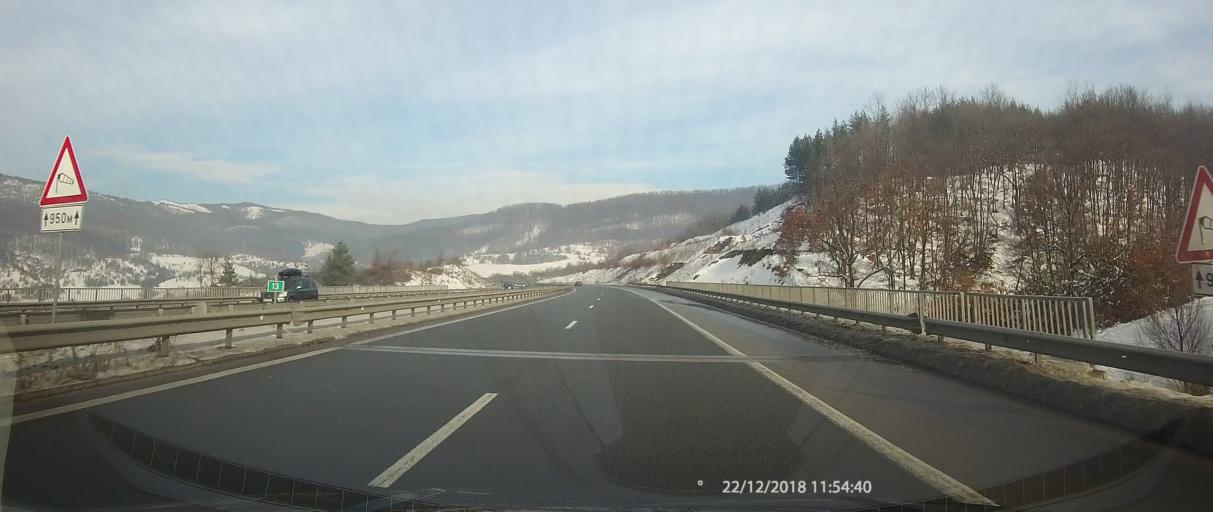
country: BG
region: Pernik
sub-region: Obshtina Pernik
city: Pernik
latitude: 42.6425
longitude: 23.1303
